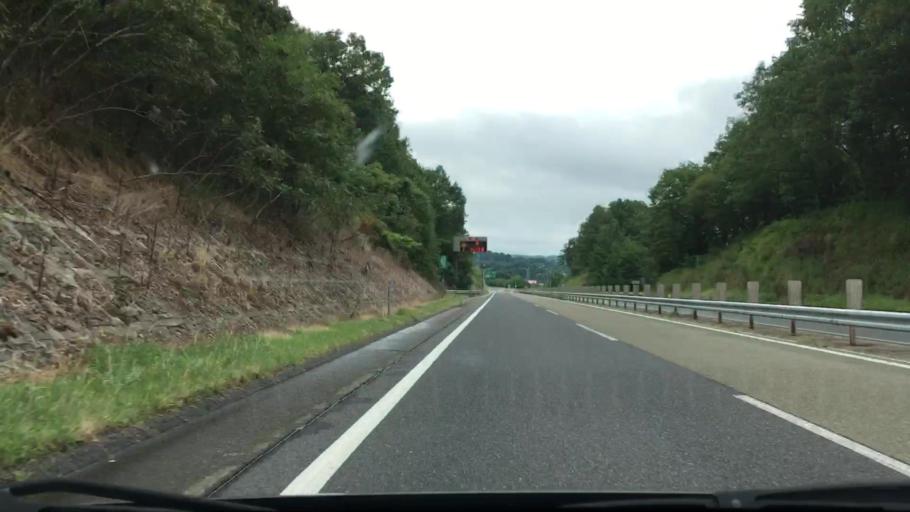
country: JP
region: Hiroshima
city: Shobara
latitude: 34.8444
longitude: 133.0305
